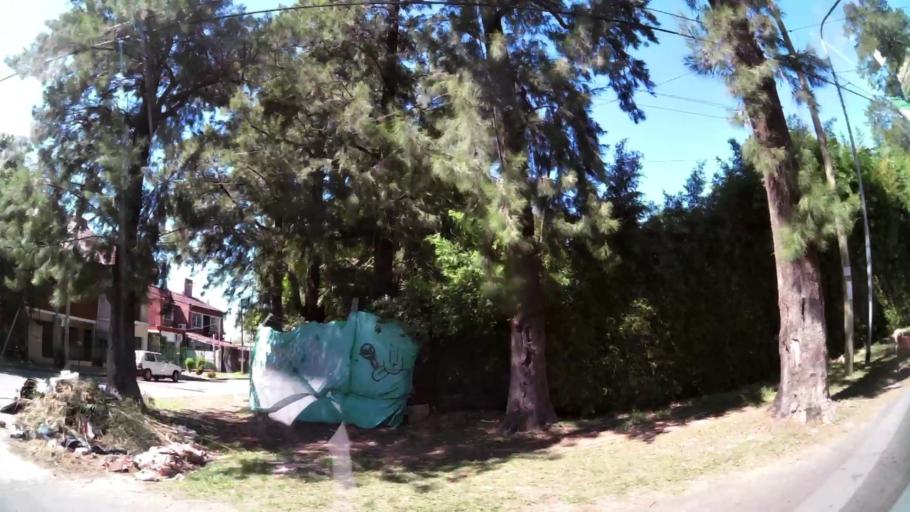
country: AR
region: Buenos Aires
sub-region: Partido de Tigre
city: Tigre
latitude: -34.5013
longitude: -58.6143
